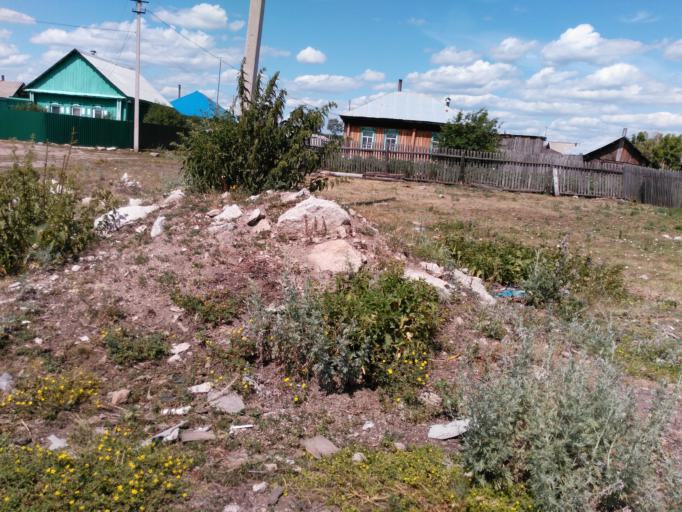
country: RU
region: Bashkortostan
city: Akhunovo
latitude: 54.2058
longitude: 59.6042
